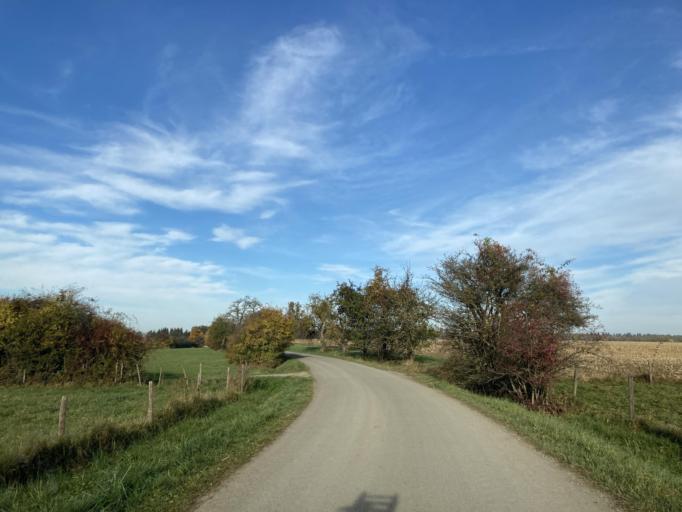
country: DE
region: Baden-Wuerttemberg
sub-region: Tuebingen Region
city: Bodelshausen
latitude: 48.3955
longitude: 8.9863
